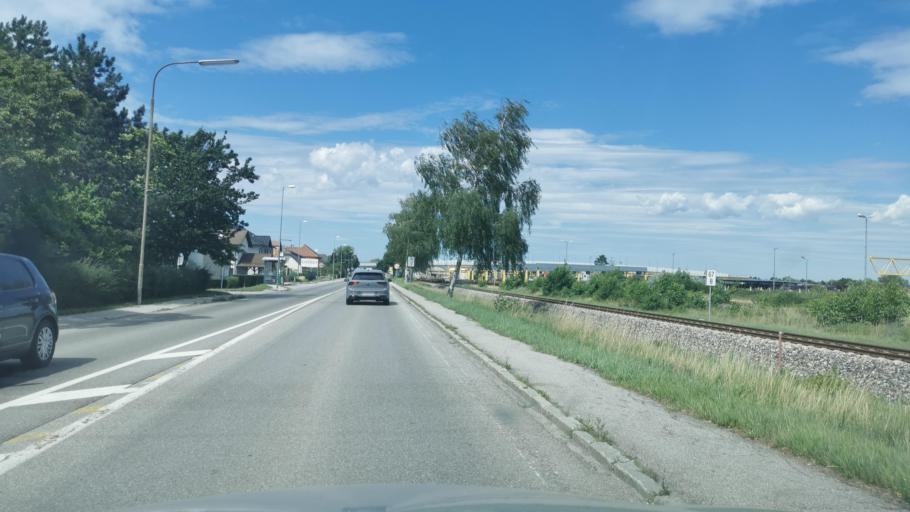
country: AT
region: Lower Austria
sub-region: Politischer Bezirk Sankt Polten
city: Wilhelmsburg
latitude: 48.1487
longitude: 15.6141
